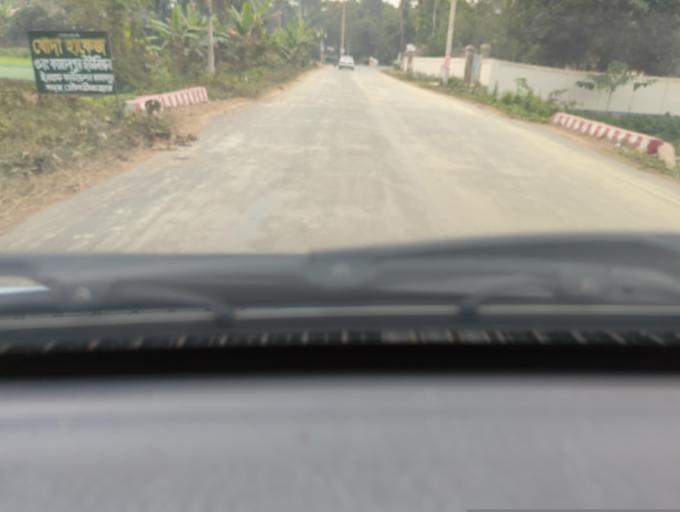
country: BD
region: Sylhet
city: Maulavi Bazar
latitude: 24.5188
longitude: 91.7302
